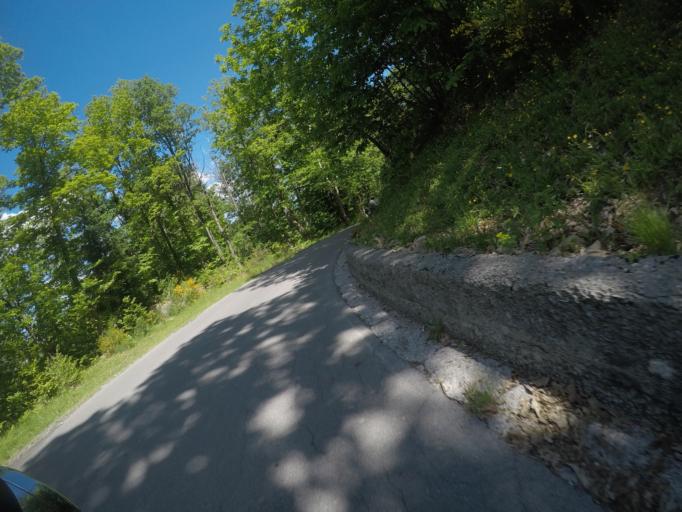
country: IT
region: Tuscany
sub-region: Provincia di Lucca
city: Careggine
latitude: 44.1112
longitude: 10.3313
